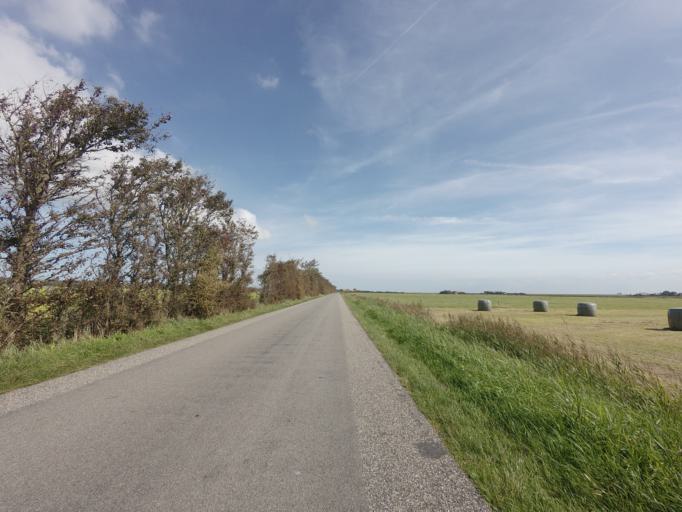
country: NL
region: Friesland
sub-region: Gemeente Ameland
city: Hollum
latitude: 53.4416
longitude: 5.6948
